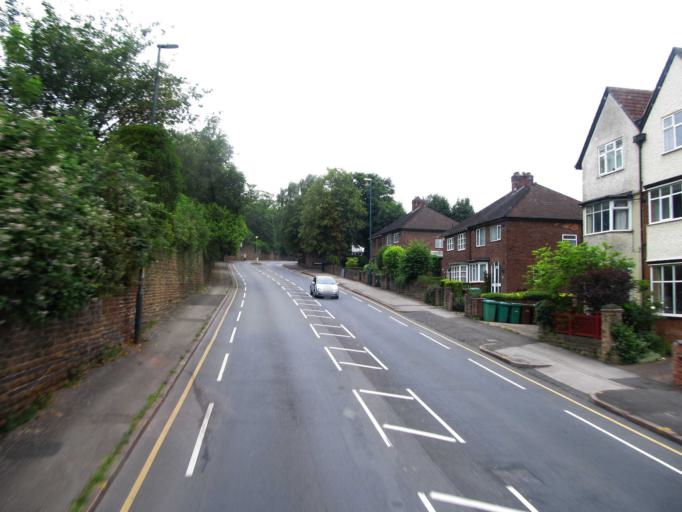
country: GB
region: England
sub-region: Nottingham
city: Nottingham
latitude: 52.9716
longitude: -1.1406
